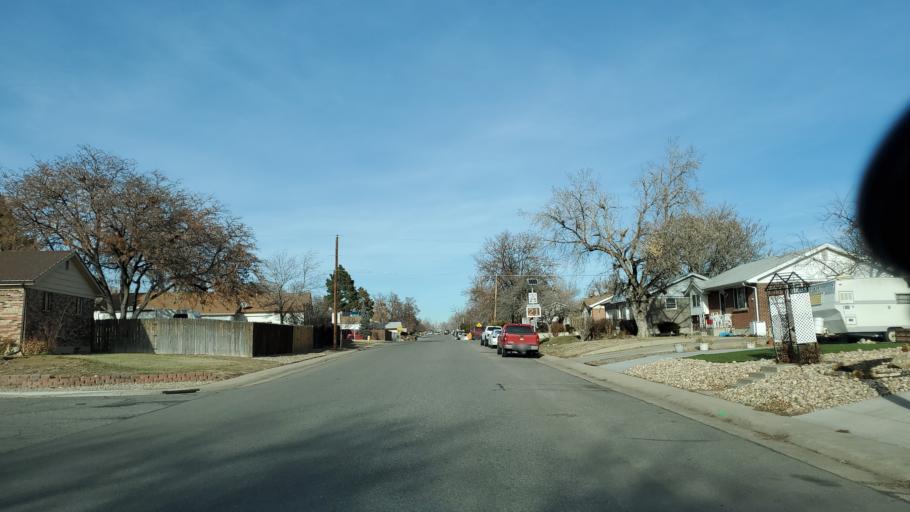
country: US
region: Colorado
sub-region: Adams County
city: Northglenn
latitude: 39.9041
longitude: -104.9608
